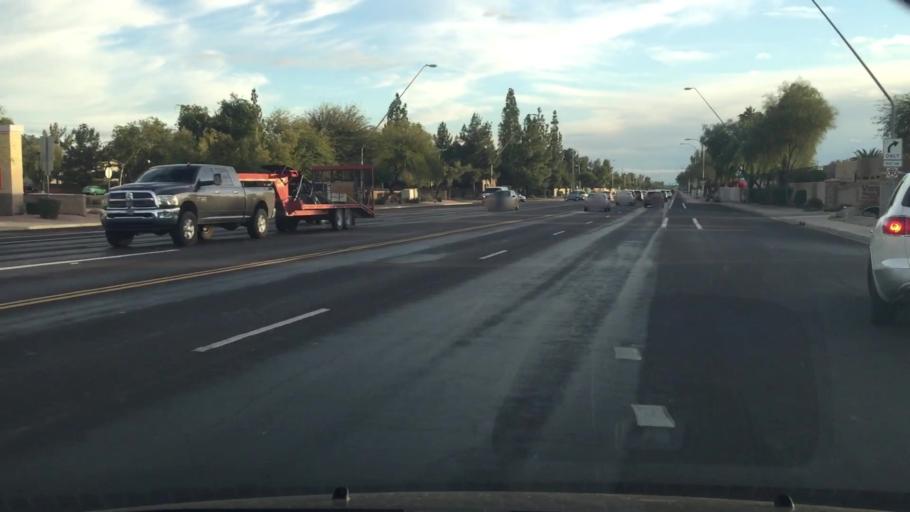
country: US
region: Arizona
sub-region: Maricopa County
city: Gilbert
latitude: 33.4079
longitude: -111.7539
